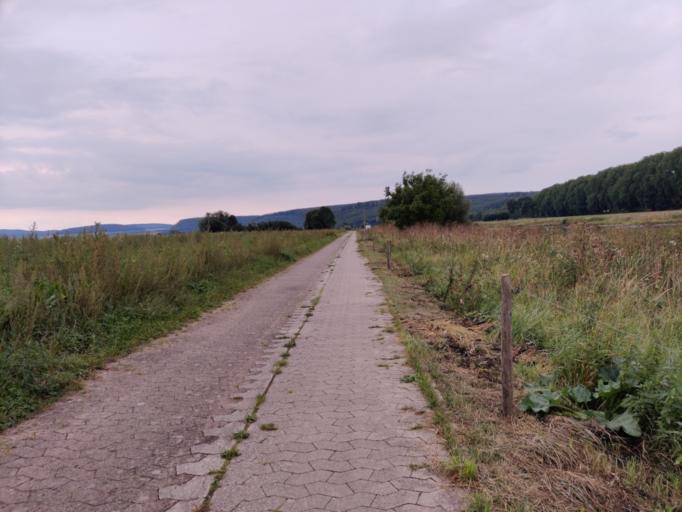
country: DE
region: Lower Saxony
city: Hehlen
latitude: 52.0145
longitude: 9.4265
